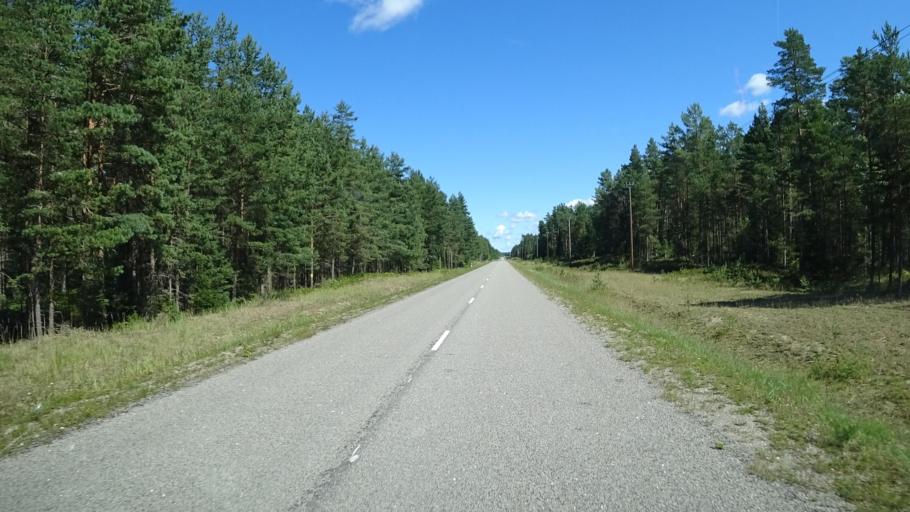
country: LV
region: Dundaga
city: Dundaga
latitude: 57.5842
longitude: 21.9672
